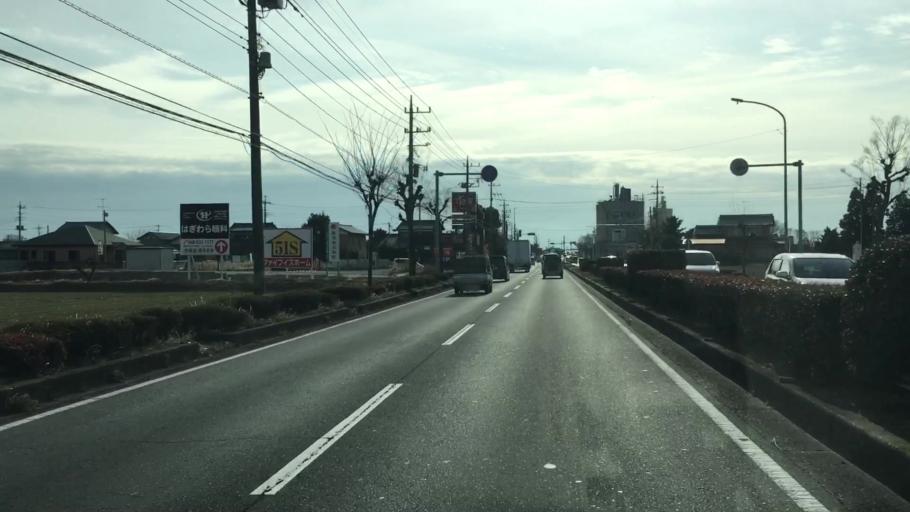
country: JP
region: Saitama
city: Menuma
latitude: 36.2124
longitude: 139.3695
